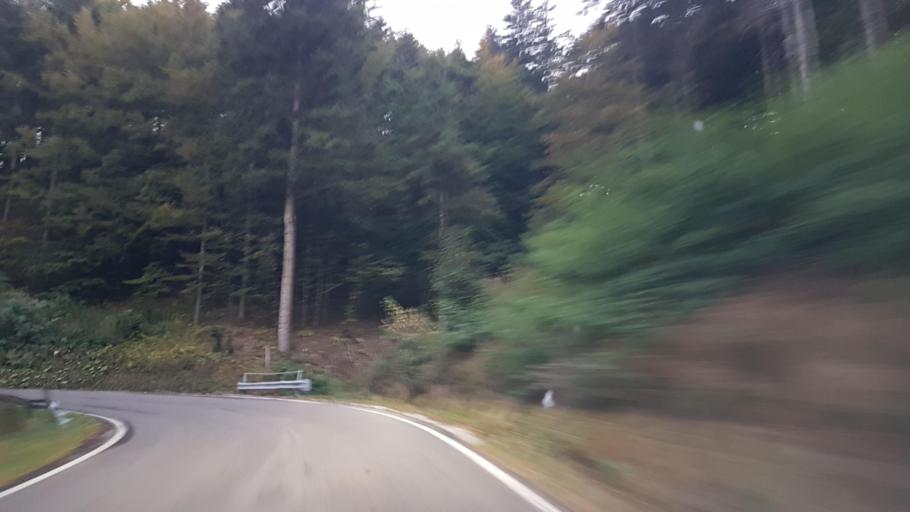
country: IT
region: Liguria
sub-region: Provincia di La Spezia
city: Varese Ligure
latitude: 44.4246
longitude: 9.6224
